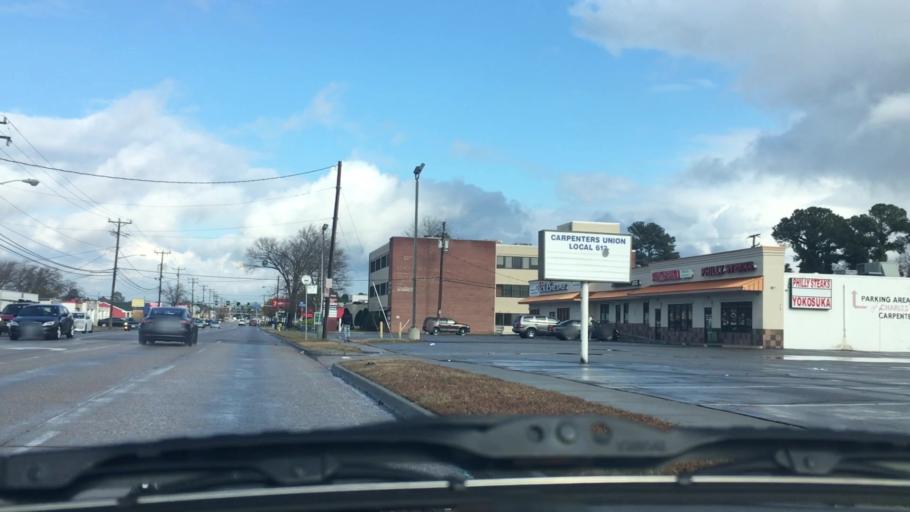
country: US
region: Virginia
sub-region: City of Norfolk
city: Norfolk
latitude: 36.9099
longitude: -76.2560
